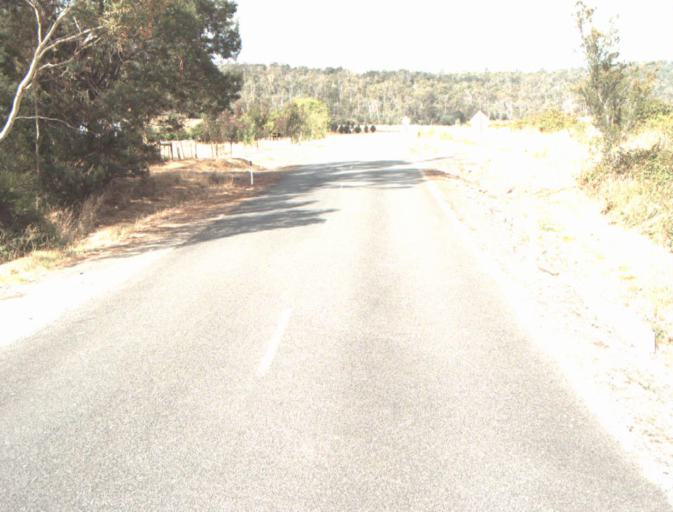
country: AU
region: Tasmania
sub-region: Launceston
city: Mayfield
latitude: -41.3104
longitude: 147.0482
